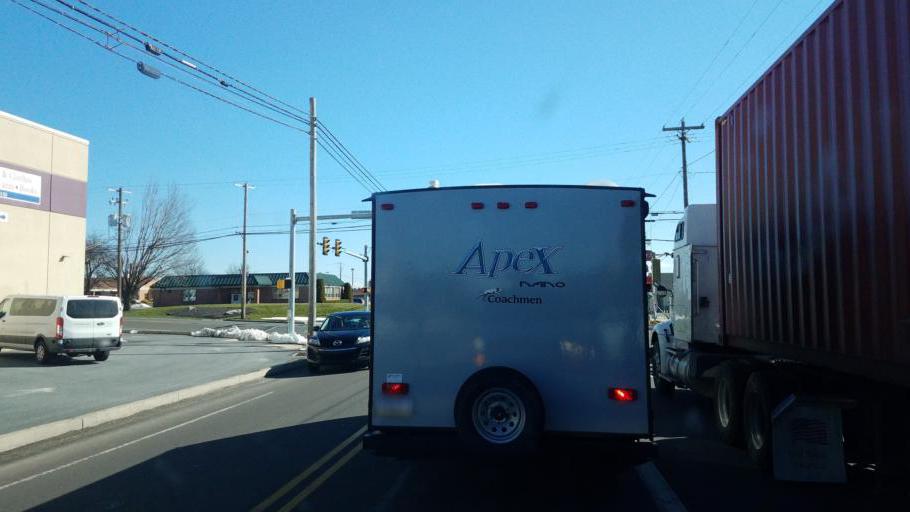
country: US
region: Pennsylvania
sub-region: Lancaster County
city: New Holland
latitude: 40.0942
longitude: -76.1132
